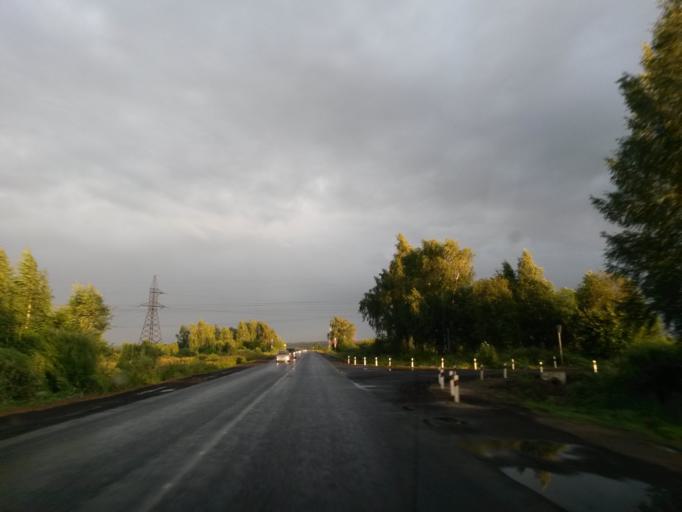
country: RU
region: Jaroslavl
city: Yaroslavl
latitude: 57.5287
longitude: 39.8772
